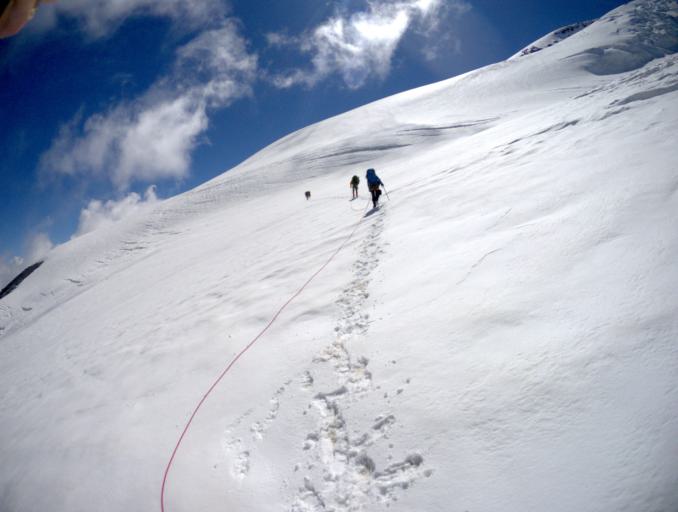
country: RU
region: Kabardino-Balkariya
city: Terskol
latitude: 43.3818
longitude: 42.4391
